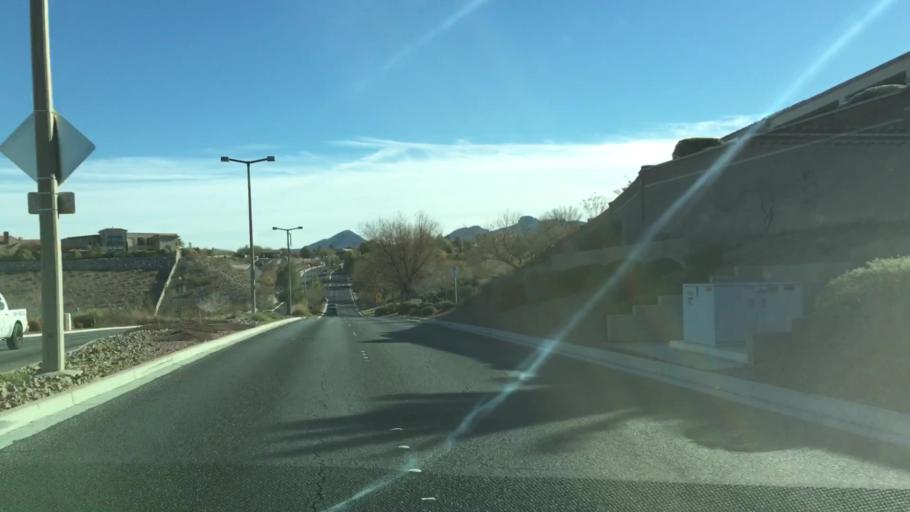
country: US
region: Nevada
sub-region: Clark County
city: Whitney
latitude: 35.9693
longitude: -115.1082
